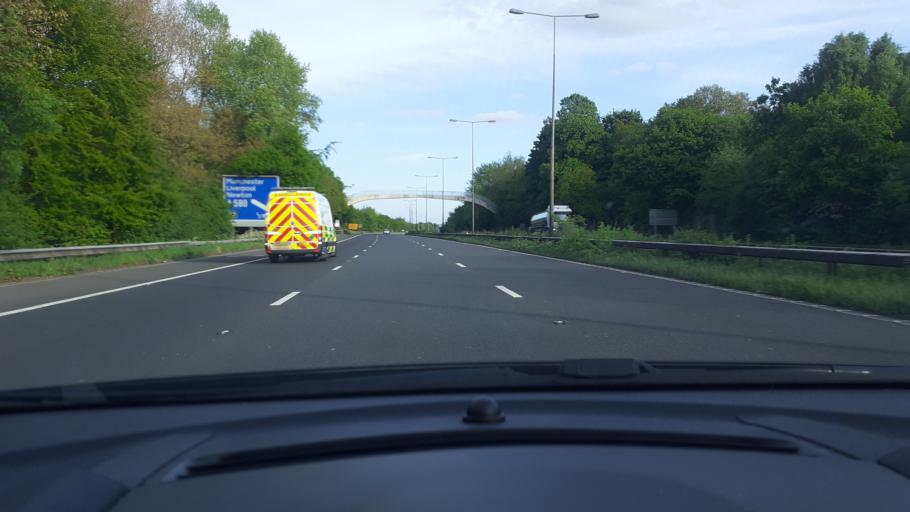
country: GB
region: England
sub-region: Borough of Wigan
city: Ashton in Makerfield
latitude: 53.4814
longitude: -2.6458
